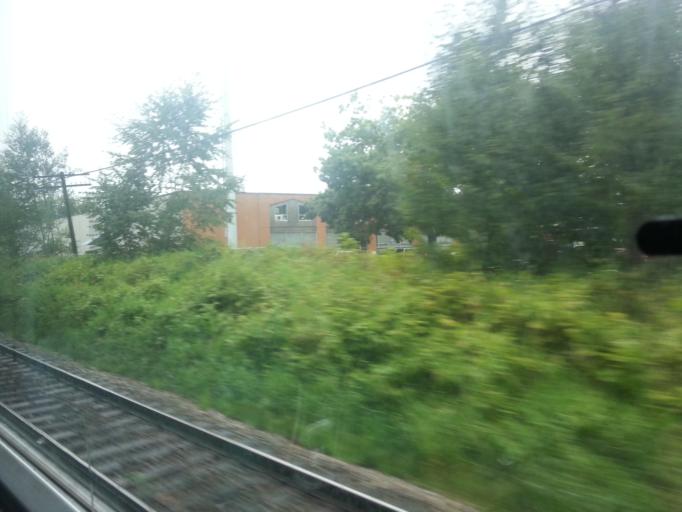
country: CA
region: British Columbia
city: Burnaby
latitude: 49.2452
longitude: -122.9365
